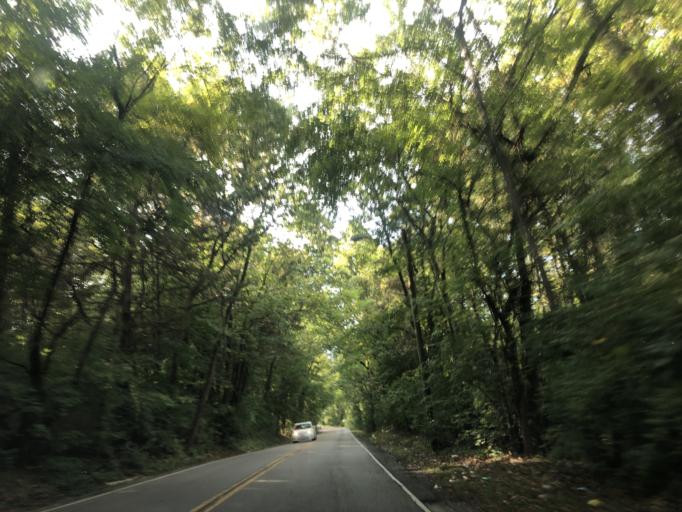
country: US
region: Tennessee
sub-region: Rutherford County
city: La Vergne
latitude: 36.0773
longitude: -86.6729
